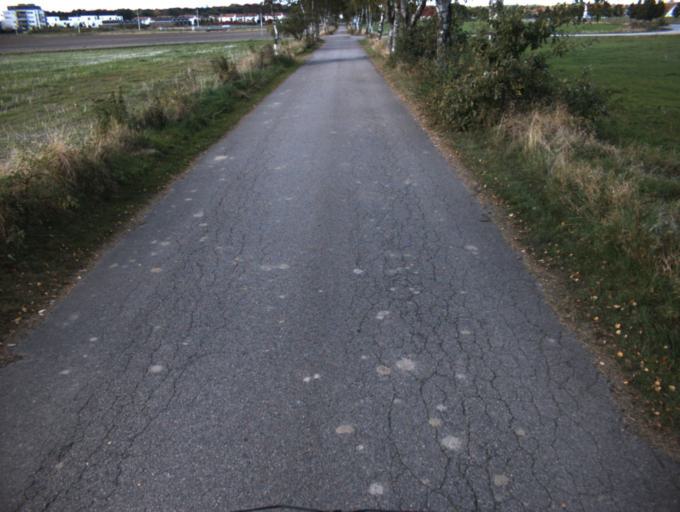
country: SE
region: Skane
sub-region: Helsingborg
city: Odakra
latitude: 56.0798
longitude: 12.7076
